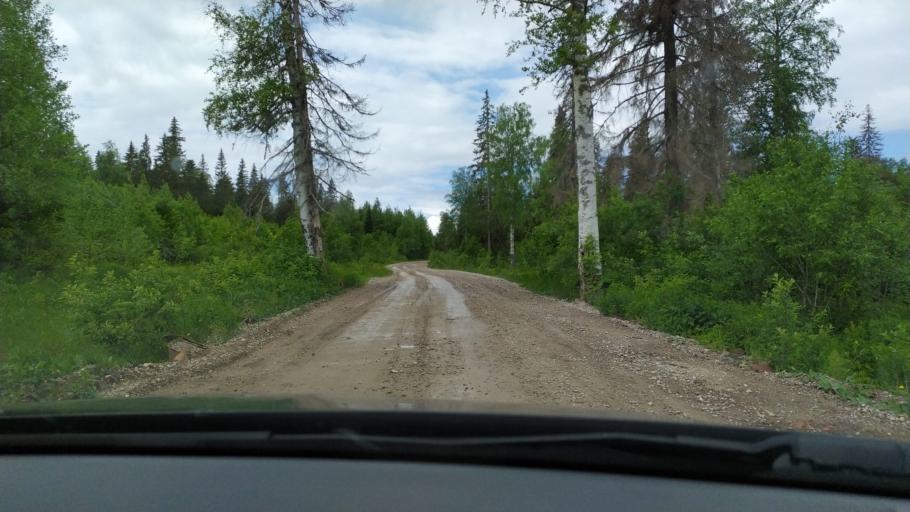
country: RU
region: Perm
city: Gremyachinsk
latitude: 58.5106
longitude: 57.8198
